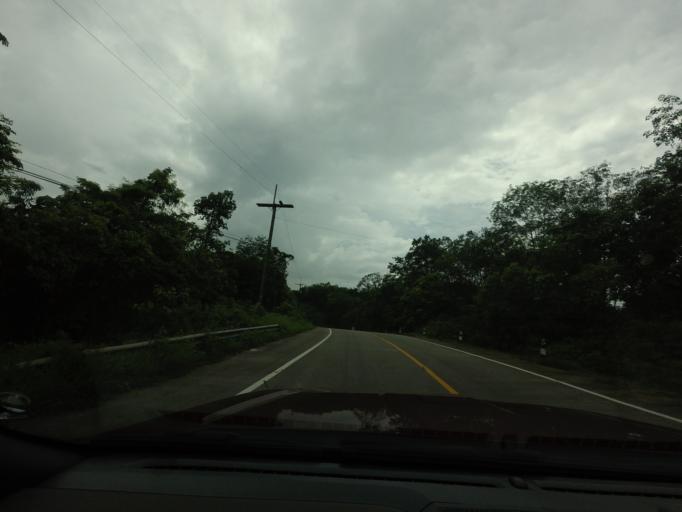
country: TH
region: Narathiwat
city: Sukhirin
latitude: 5.9795
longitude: 101.7013
